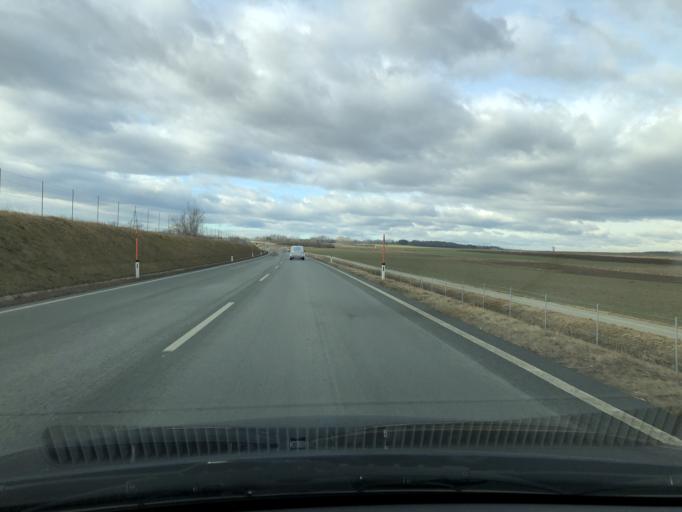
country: AT
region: Burgenland
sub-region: Politischer Bezirk Oberwart
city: Markt Neuhodis
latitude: 47.2754
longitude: 16.3988
